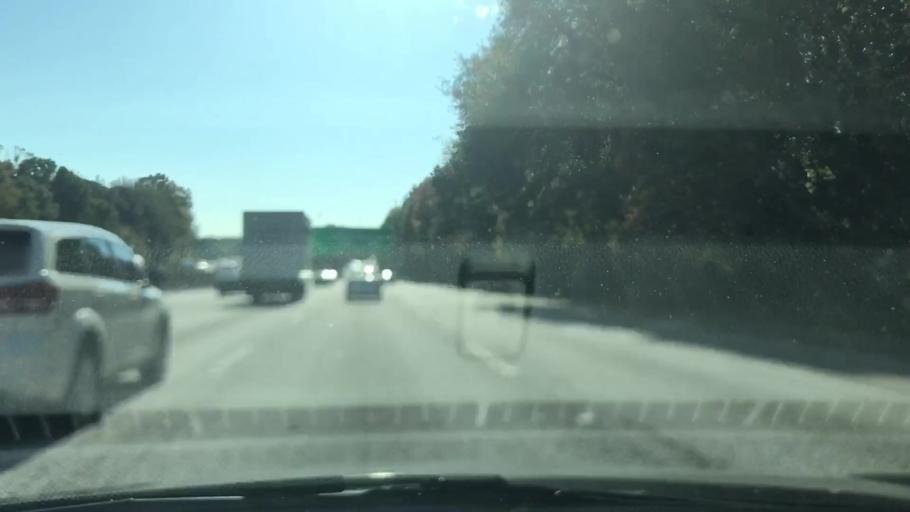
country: US
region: Georgia
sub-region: DeKalb County
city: Candler-McAfee
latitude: 33.7230
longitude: -84.2361
